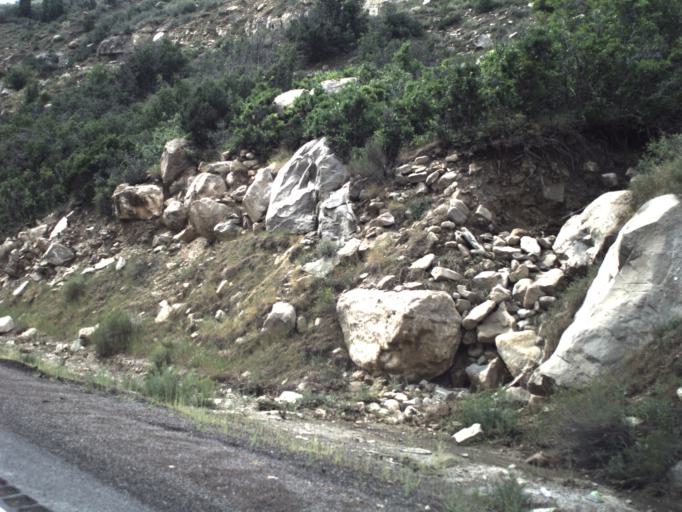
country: US
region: Utah
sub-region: Carbon County
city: Helper
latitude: 39.7773
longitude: -110.9160
